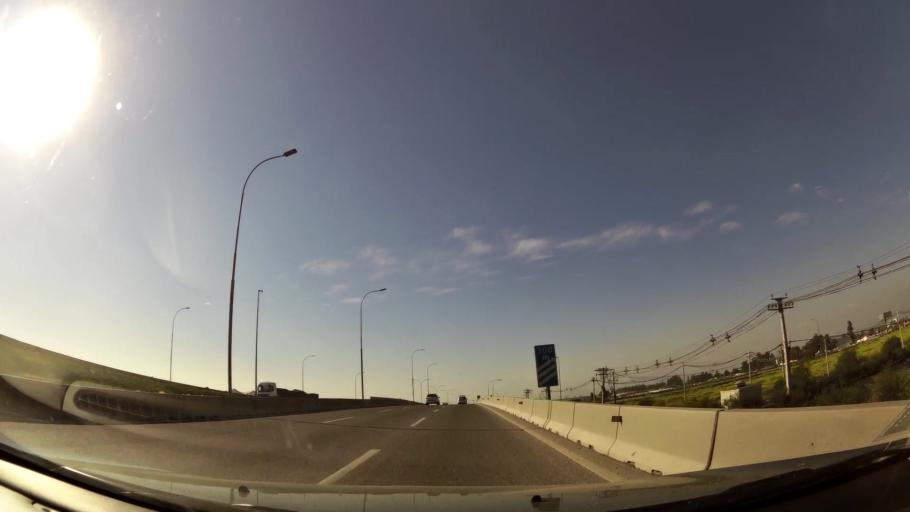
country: CL
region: Santiago Metropolitan
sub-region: Provincia de Maipo
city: San Bernardo
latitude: -33.5540
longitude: -70.7093
